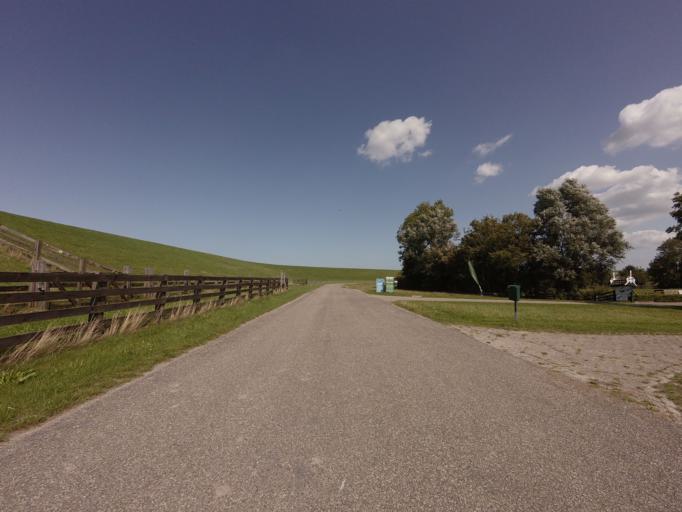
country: NL
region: Friesland
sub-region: Gemeente Ferwerderadiel
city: Hallum
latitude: 53.3285
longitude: 5.7712
